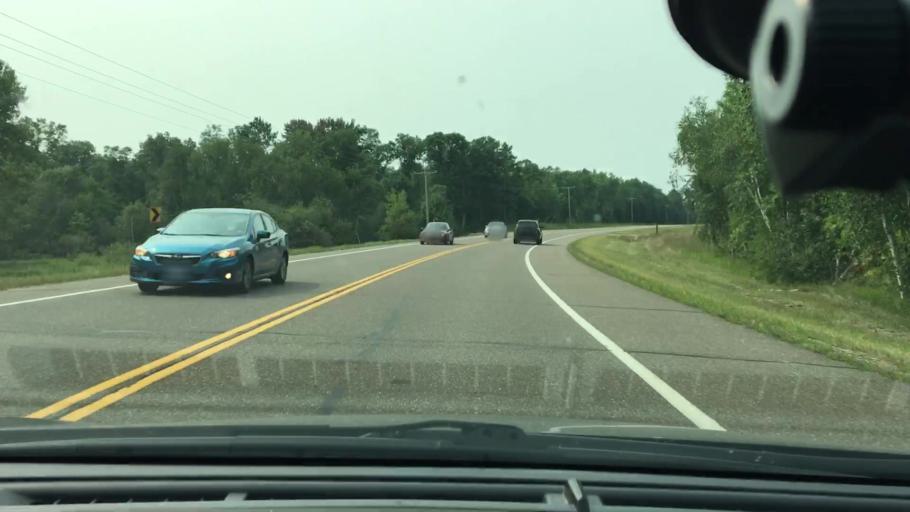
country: US
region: Minnesota
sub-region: Crow Wing County
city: Breezy Point
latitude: 46.5666
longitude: -94.1290
